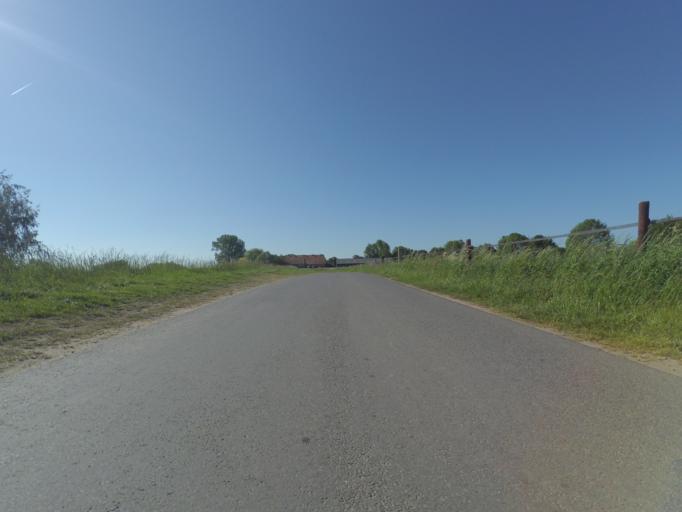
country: NL
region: Gelderland
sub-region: Gemeente Voorst
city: Wilp
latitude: 52.2244
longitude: 6.1634
